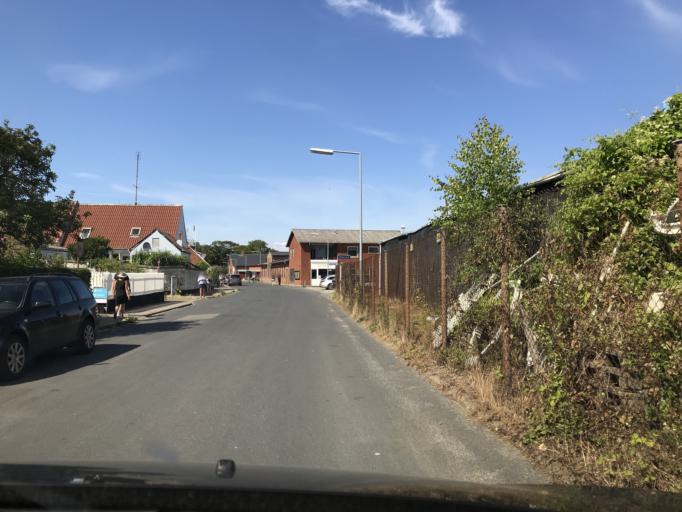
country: DK
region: South Denmark
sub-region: AEro Kommune
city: Marstal
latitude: 54.8524
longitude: 10.5217
